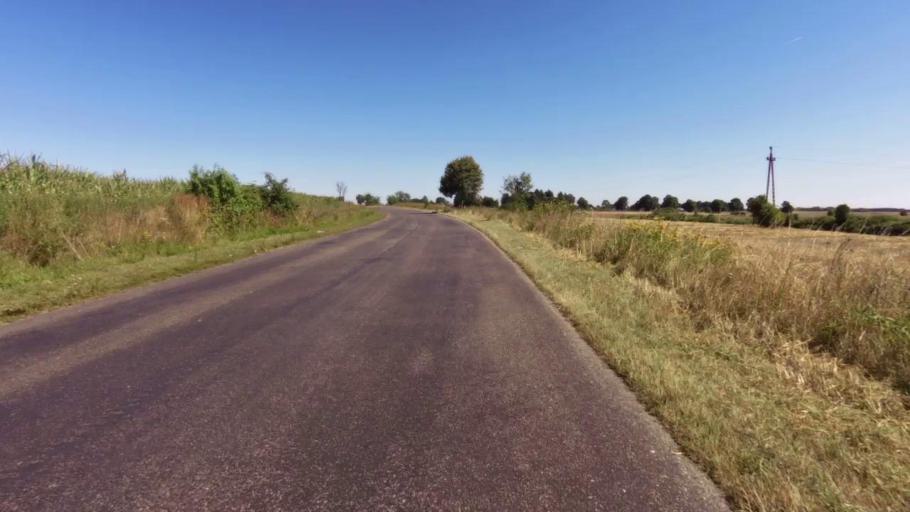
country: PL
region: West Pomeranian Voivodeship
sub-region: Powiat szczecinecki
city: Lubowo
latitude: 53.5834
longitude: 16.4337
